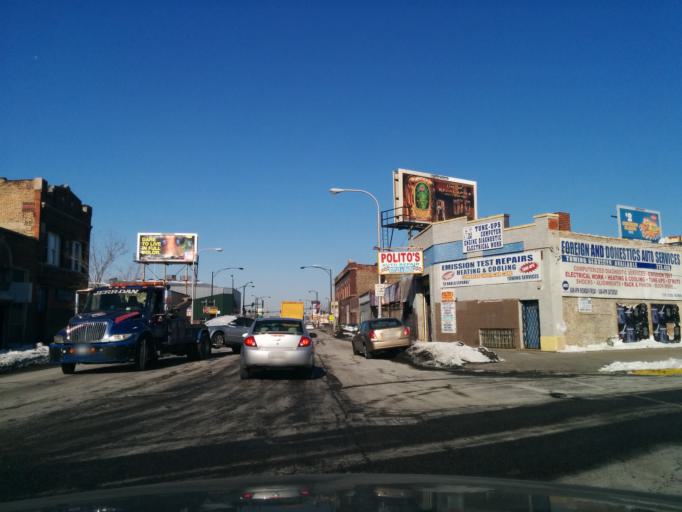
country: US
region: Illinois
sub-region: Cook County
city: Oak Park
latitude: 41.9092
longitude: -87.7338
